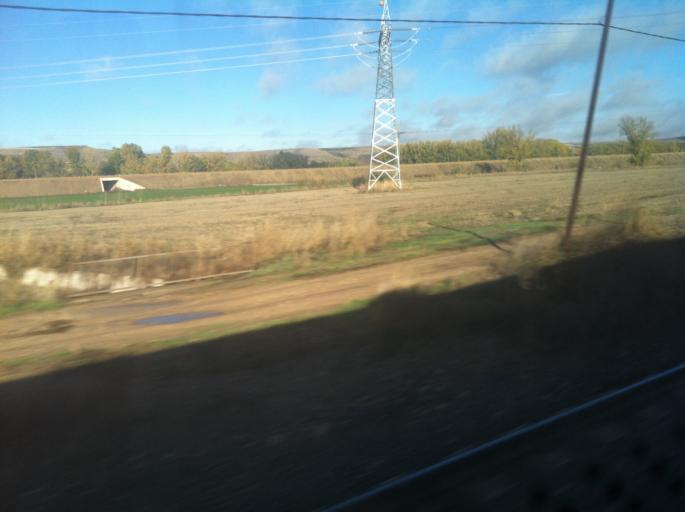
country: ES
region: Castille and Leon
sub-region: Provincia de Burgos
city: Buniel
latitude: 42.3113
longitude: -3.8249
